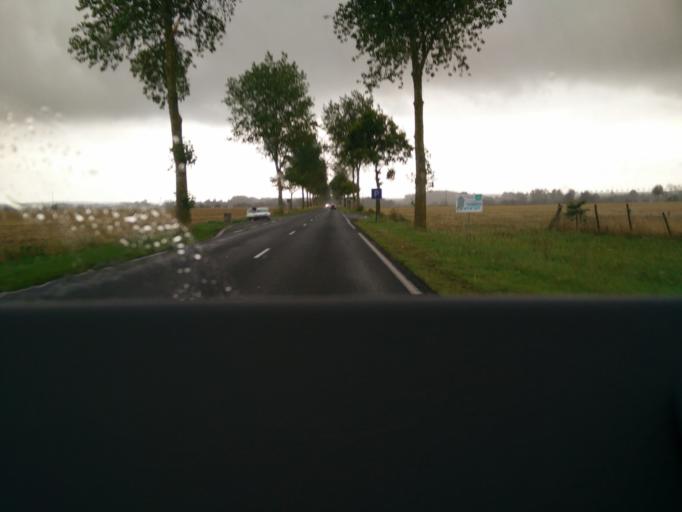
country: FR
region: Nord-Pas-de-Calais
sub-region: Departement du Pas-de-Calais
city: Savy-Berlette
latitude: 50.3497
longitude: 2.5332
